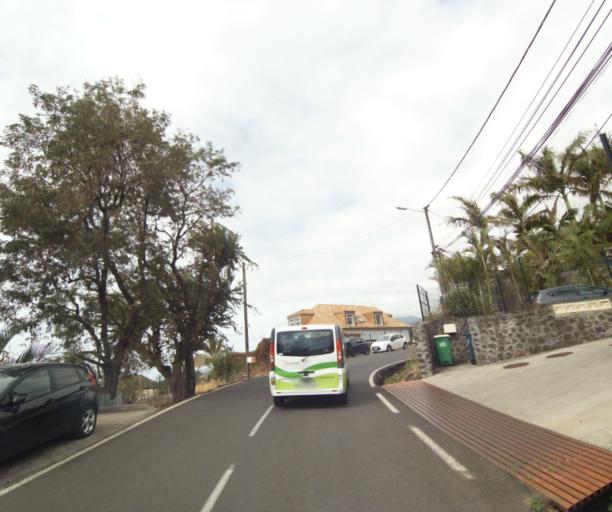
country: RE
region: Reunion
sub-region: Reunion
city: Saint-Paul
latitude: -21.0167
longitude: 55.2868
